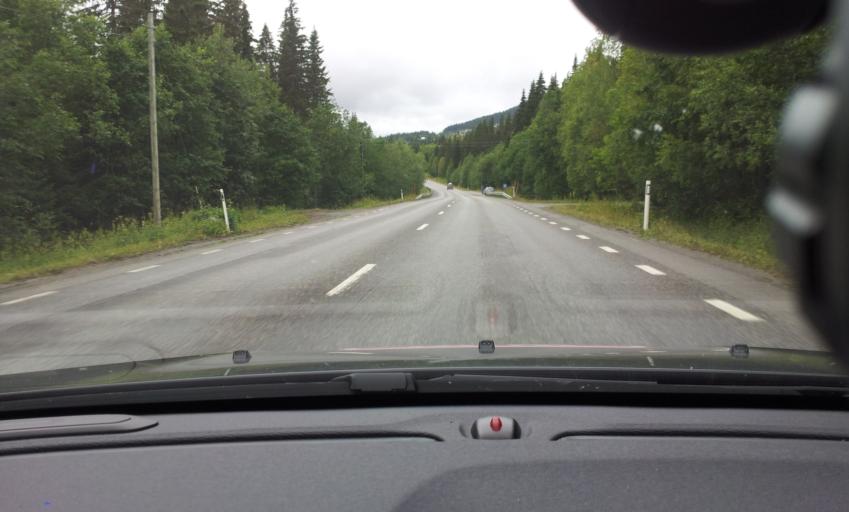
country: SE
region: Jaemtland
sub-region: Are Kommun
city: Are
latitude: 63.4027
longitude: 12.9985
